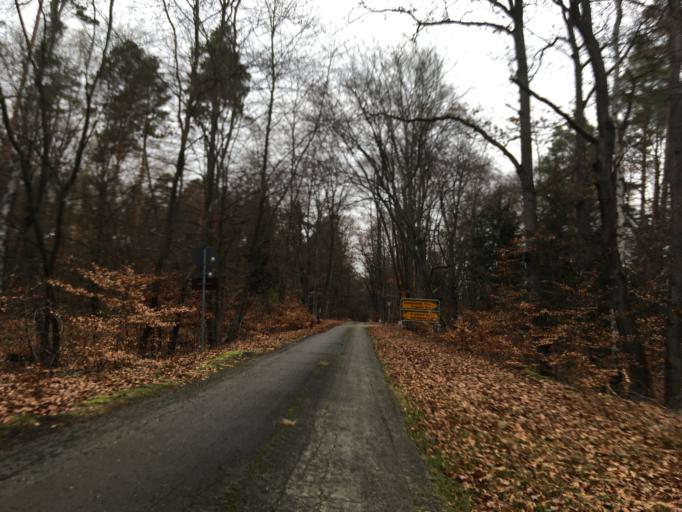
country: DE
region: Brandenburg
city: Jamlitz
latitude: 52.0807
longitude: 14.4765
